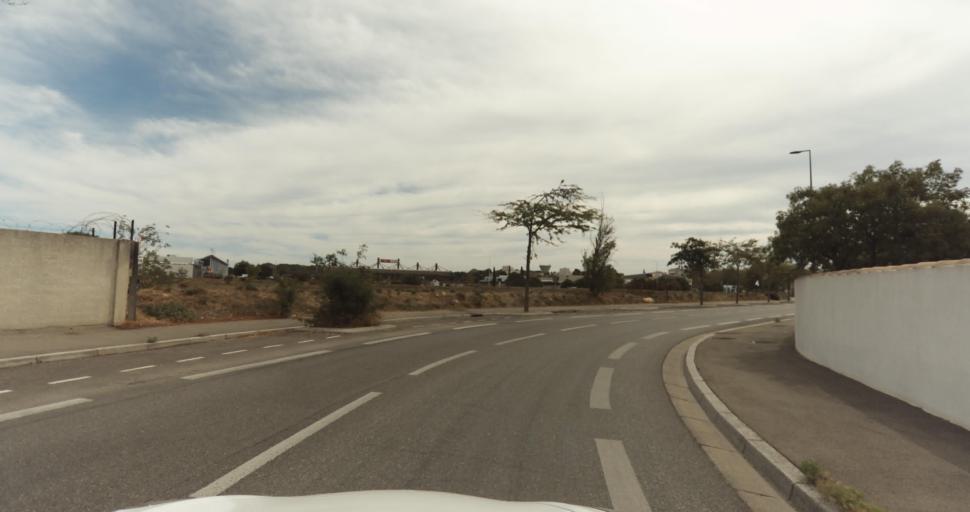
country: FR
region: Provence-Alpes-Cote d'Azur
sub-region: Departement des Bouches-du-Rhone
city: Miramas
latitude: 43.6000
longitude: 5.0006
